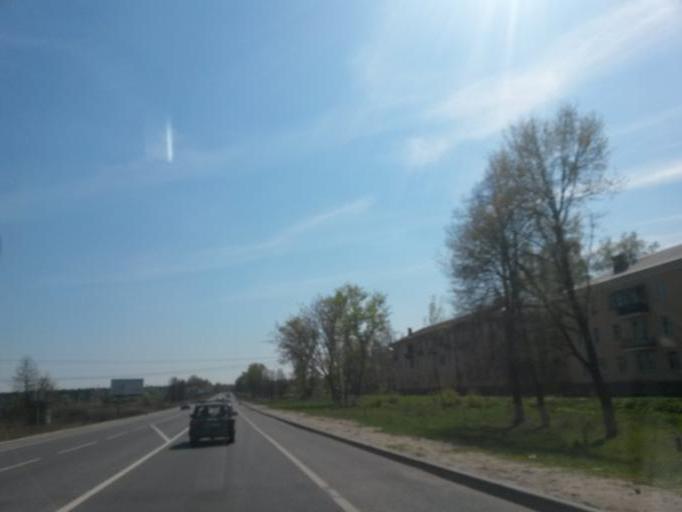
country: RU
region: Moskovskaya
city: L'vovskiy
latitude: 55.3119
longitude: 37.5287
